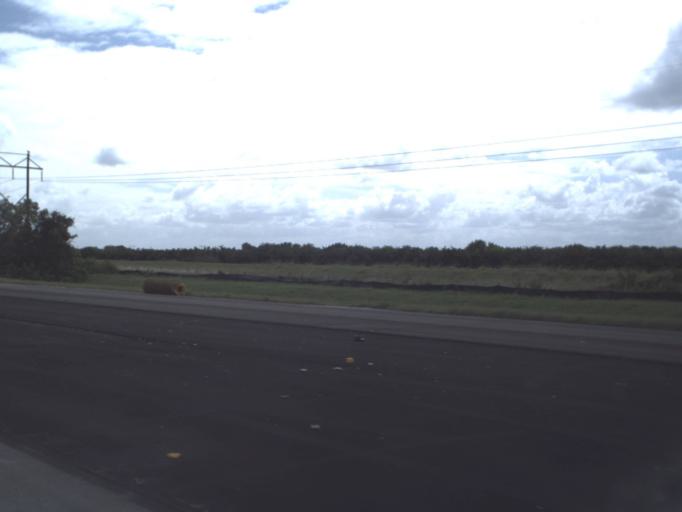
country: US
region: Florida
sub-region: Lee County
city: Lehigh Acres
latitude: 26.5131
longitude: -81.5426
